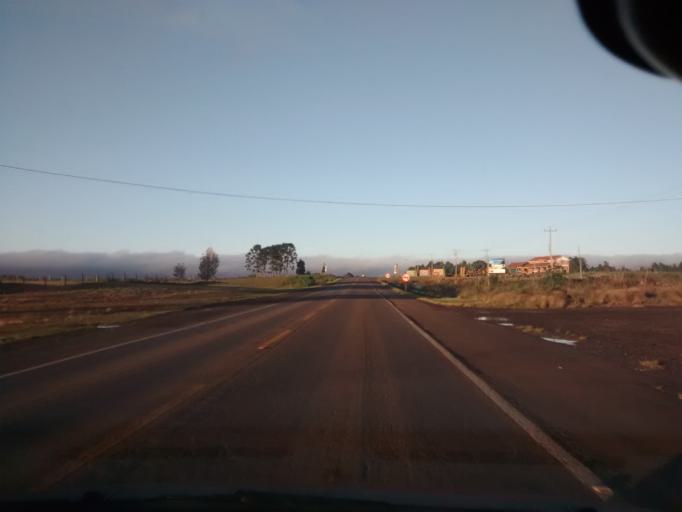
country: BR
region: Rio Grande do Sul
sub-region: Vacaria
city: Vacaria
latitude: -28.4369
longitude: -50.8742
